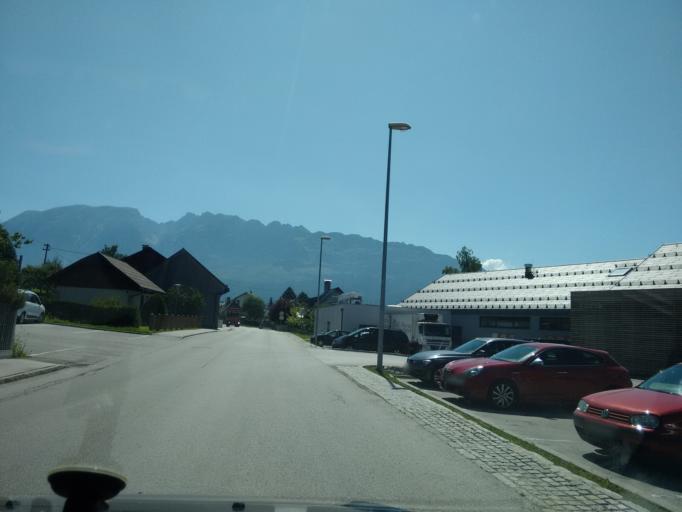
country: AT
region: Styria
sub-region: Politischer Bezirk Liezen
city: Tauplitz
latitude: 47.5580
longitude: 13.9244
